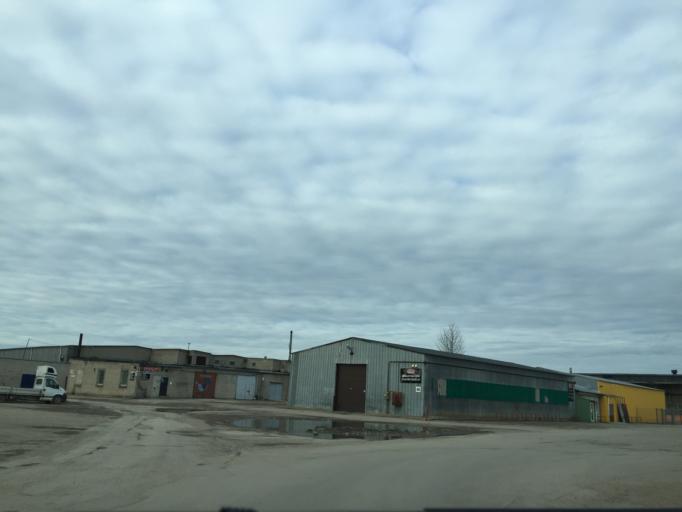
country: LT
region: Klaipedos apskritis
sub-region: Klaipeda
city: Klaipeda
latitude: 55.6972
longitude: 21.1768
